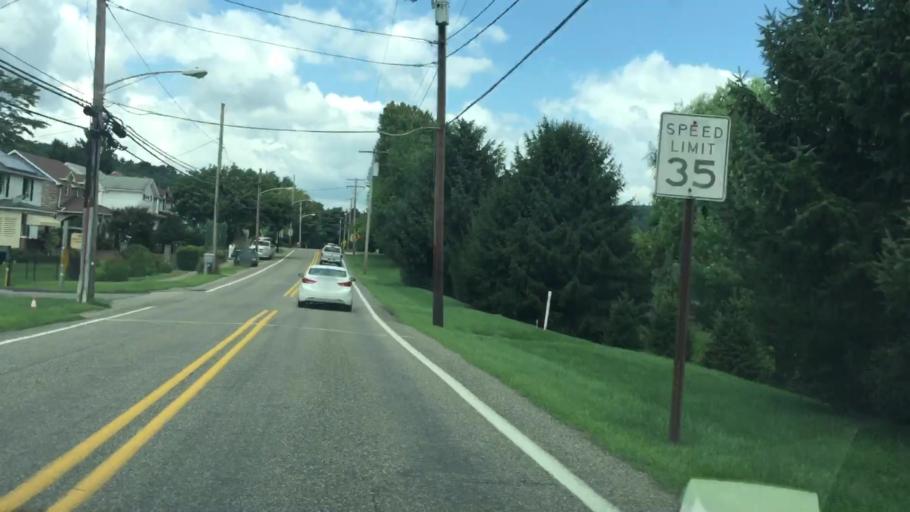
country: US
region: Pennsylvania
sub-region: Allegheny County
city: Cheswick
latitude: 40.5507
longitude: -79.8050
